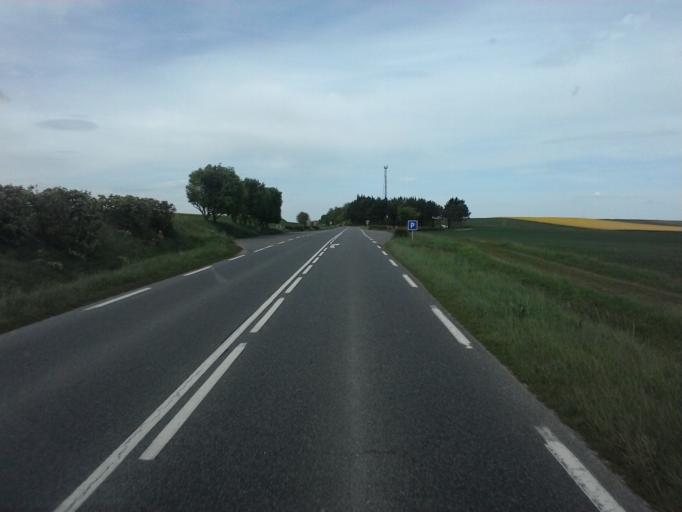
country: FR
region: Champagne-Ardenne
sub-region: Departement de l'Aube
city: Bouilly
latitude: 48.1580
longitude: 4.0215
